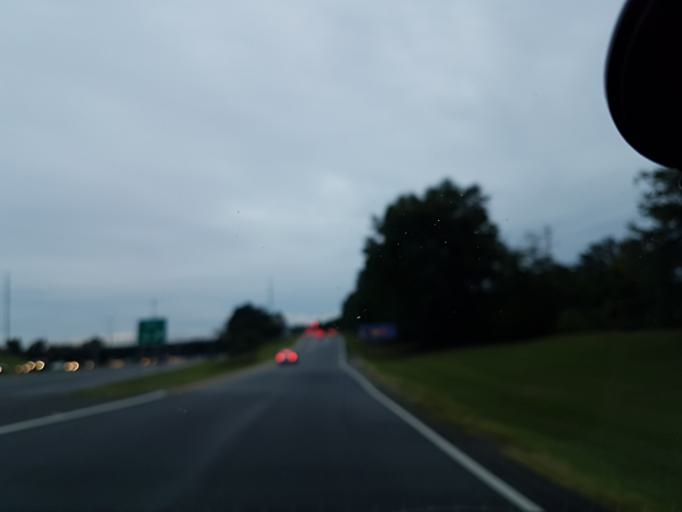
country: US
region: Georgia
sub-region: DeKalb County
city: Tucker
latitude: 33.8347
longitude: -84.2028
